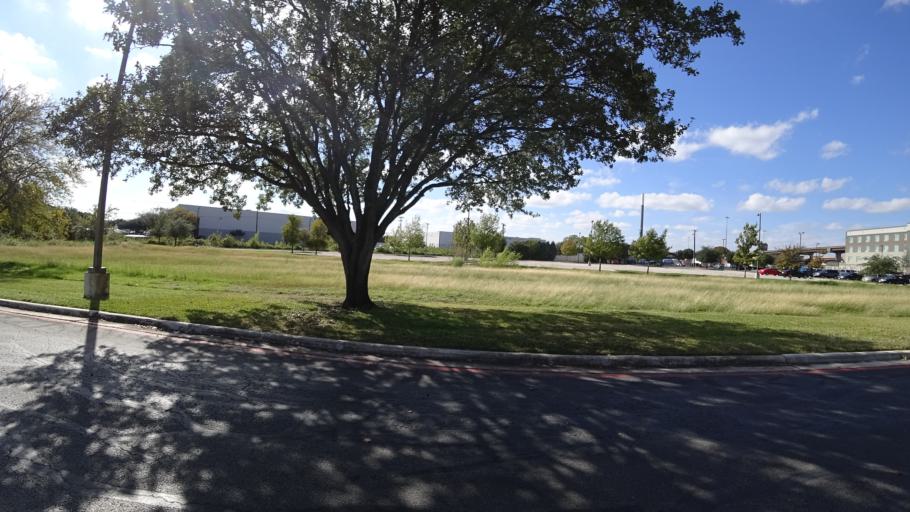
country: US
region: Texas
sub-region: Williamson County
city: Round Rock
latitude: 30.4779
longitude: -97.6760
